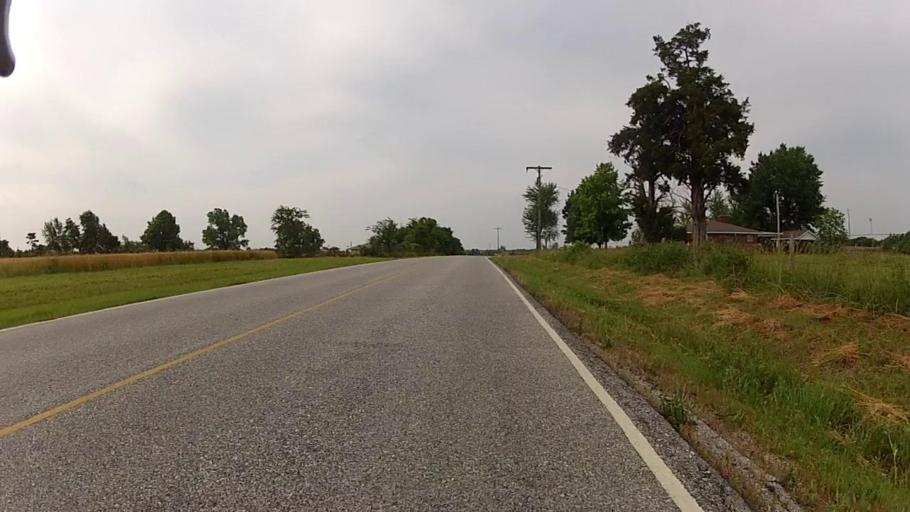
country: US
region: Kansas
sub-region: Cherokee County
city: Baxter Springs
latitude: 37.0803
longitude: -94.7223
